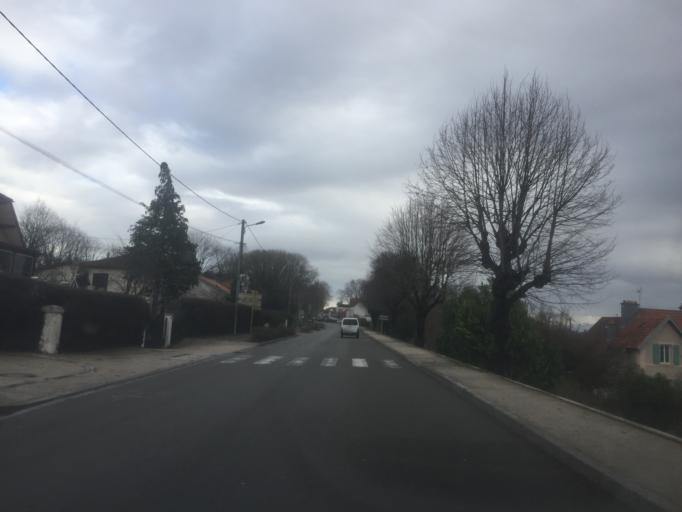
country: FR
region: Franche-Comte
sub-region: Departement du Doubs
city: Saint-Vit
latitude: 47.1791
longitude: 5.8008
